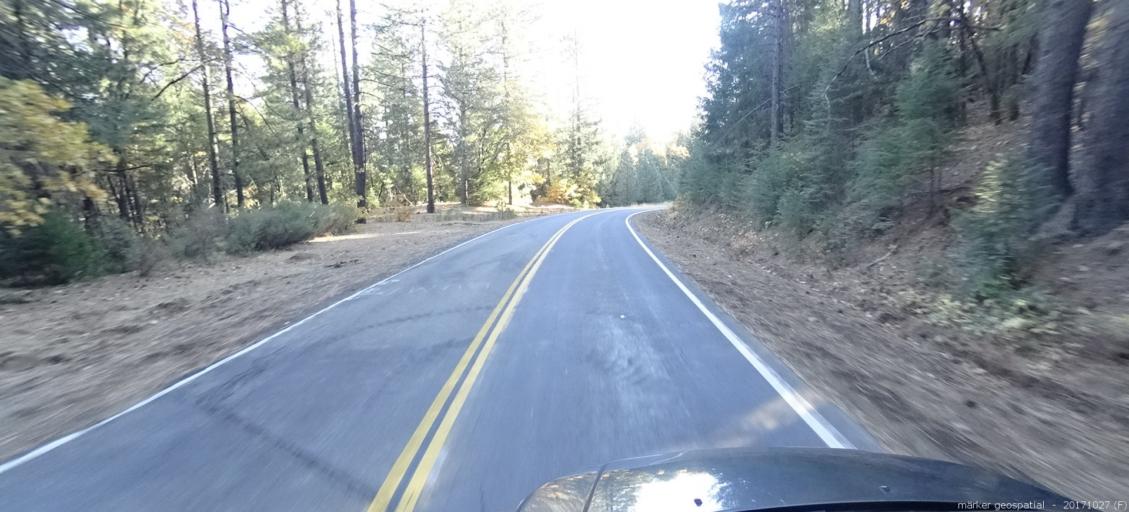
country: US
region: California
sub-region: Shasta County
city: Burney
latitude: 40.9906
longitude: -121.9248
